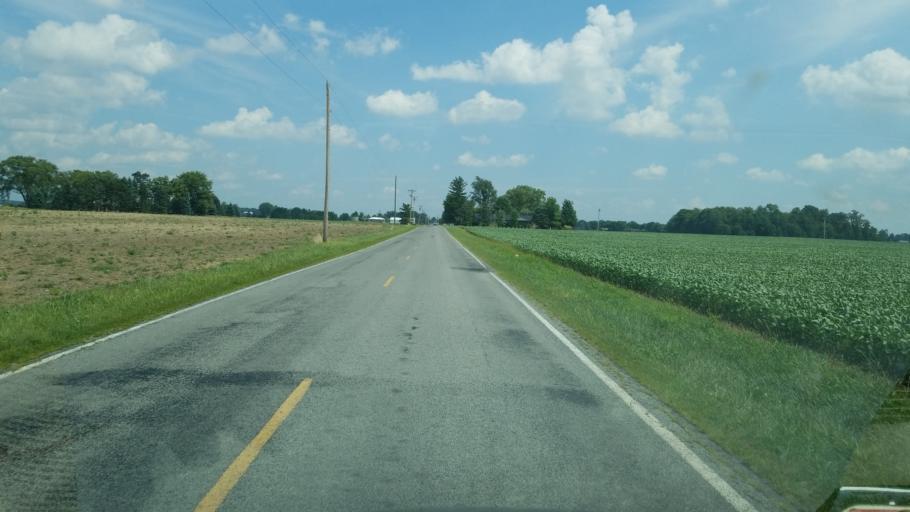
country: US
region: Ohio
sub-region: Hancock County
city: Arlington
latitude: 40.9068
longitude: -83.6649
